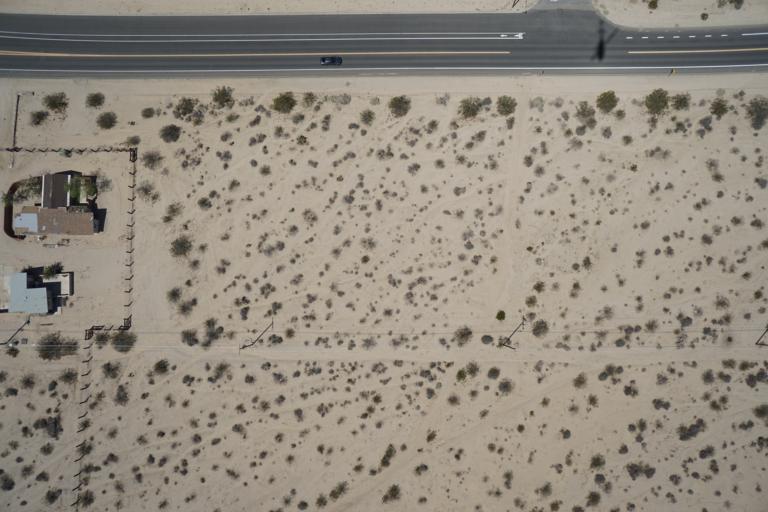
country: US
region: California
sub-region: San Bernardino County
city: Twentynine Palms
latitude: 34.1311
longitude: -116.0360
